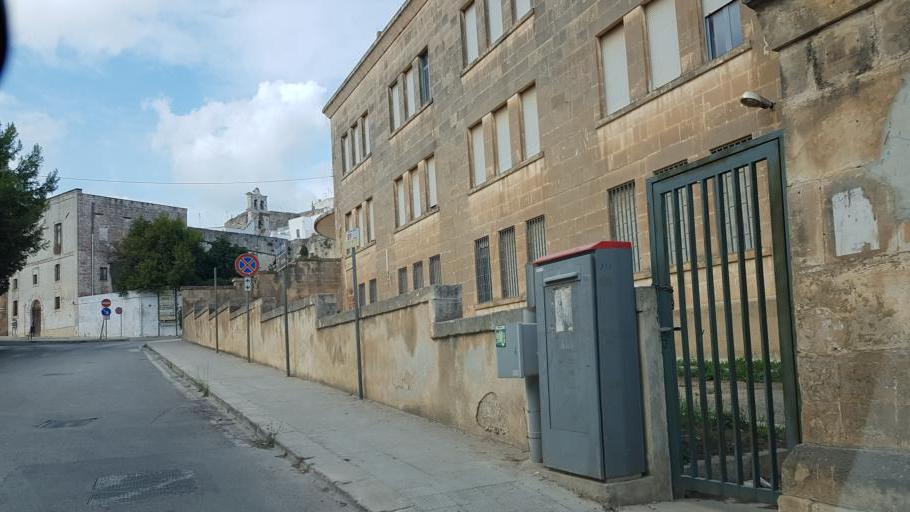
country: IT
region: Apulia
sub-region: Provincia di Brindisi
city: Ostuni
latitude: 40.7329
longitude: 17.5814
